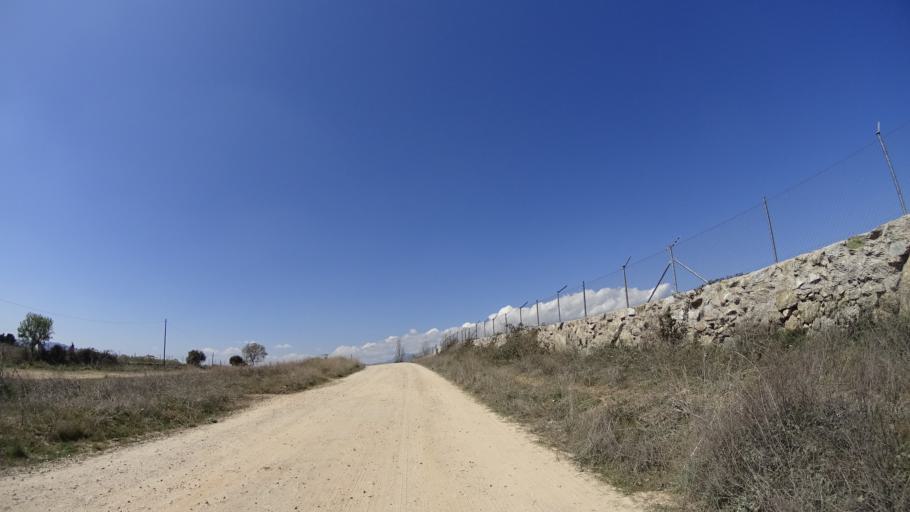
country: ES
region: Madrid
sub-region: Provincia de Madrid
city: Colmenar Viejo
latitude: 40.6868
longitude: -3.7619
